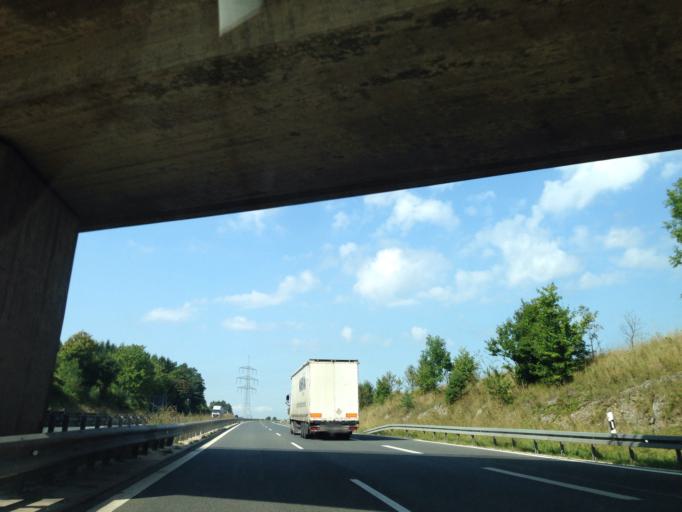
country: DE
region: Bavaria
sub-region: Upper Franconia
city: Wattendorf
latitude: 49.9889
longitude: 11.1201
